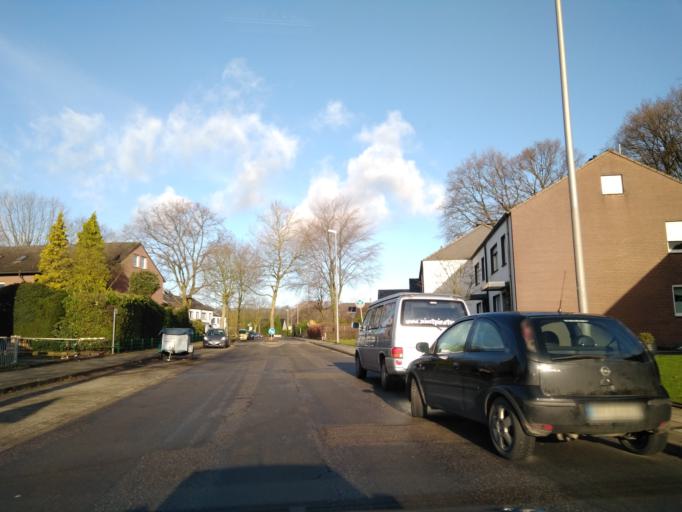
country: DE
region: North Rhine-Westphalia
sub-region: Regierungsbezirk Munster
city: Gladbeck
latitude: 51.5827
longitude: 6.9701
